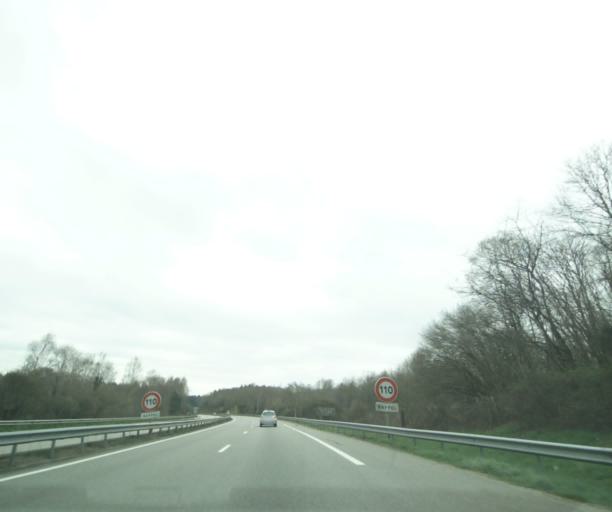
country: FR
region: Limousin
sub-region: Departement de la Haute-Vienne
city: Bonnac-la-Cote
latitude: 45.9333
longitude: 1.3033
